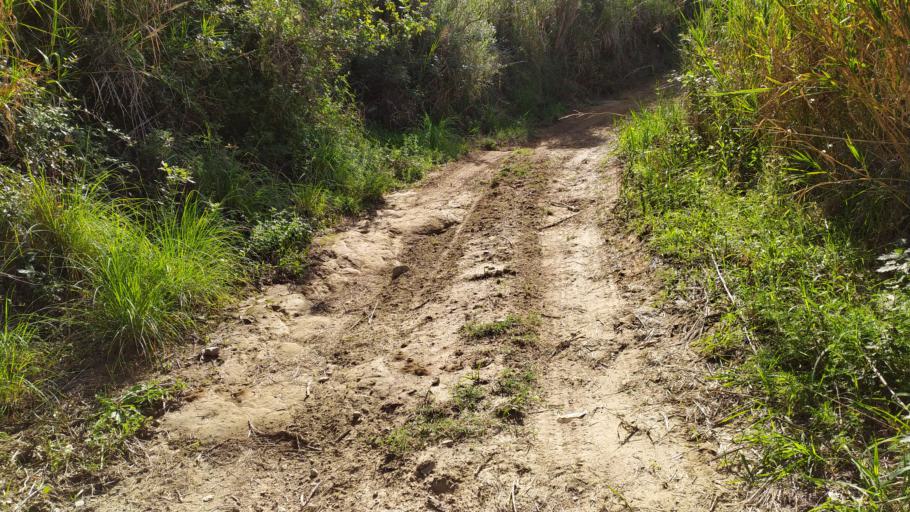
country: IT
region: Sicily
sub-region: Messina
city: Monforte San Giorgio
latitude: 38.1540
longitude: 15.3990
